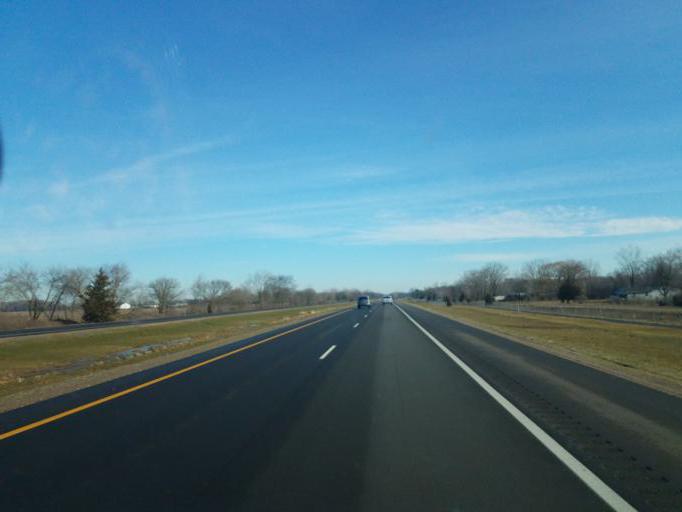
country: US
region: Michigan
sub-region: Gratiot County
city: Ithaca
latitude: 43.3438
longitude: -84.6015
